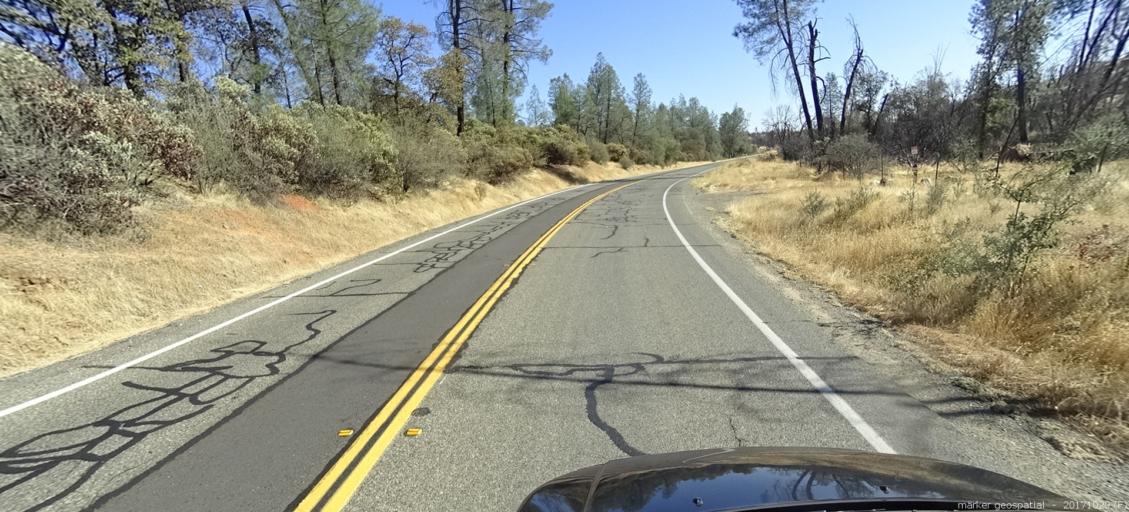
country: US
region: California
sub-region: Shasta County
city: Shasta
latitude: 40.4909
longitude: -122.5282
